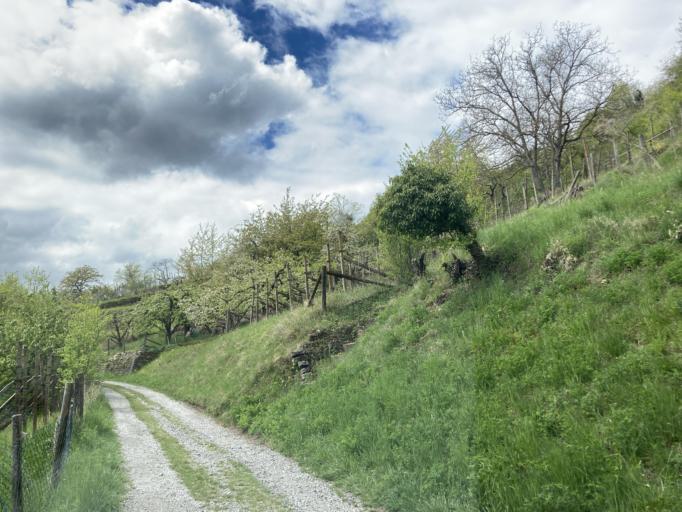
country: DE
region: Baden-Wuerttemberg
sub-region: Tuebingen Region
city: Tuebingen
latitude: 48.5047
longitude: 8.9993
